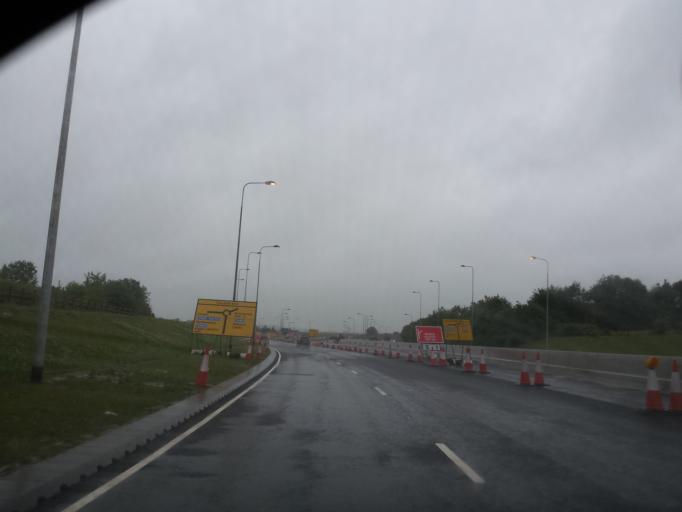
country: GB
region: England
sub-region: Warwickshire
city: Ryton on Dunsmore
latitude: 52.3808
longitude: -1.4599
